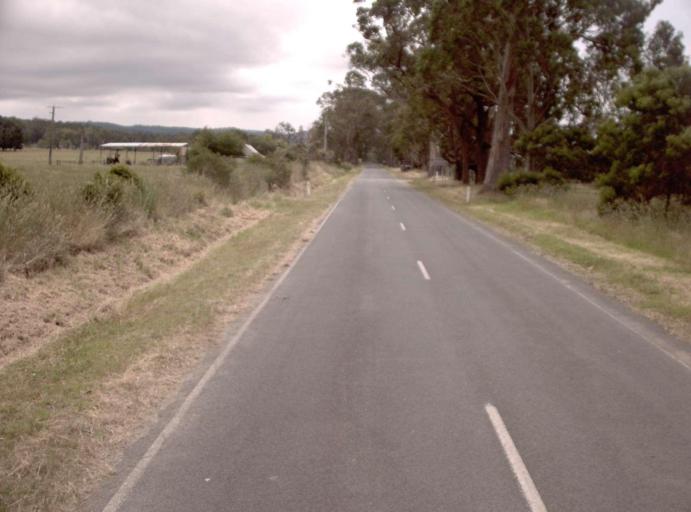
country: AU
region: Victoria
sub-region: Latrobe
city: Traralgon
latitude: -38.5166
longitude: 146.6481
